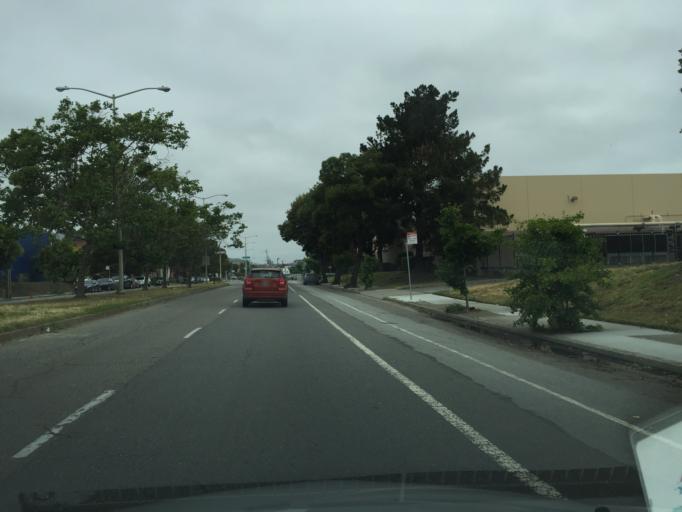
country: US
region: California
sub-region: San Francisco County
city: San Francisco
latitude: 37.7413
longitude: -122.3853
